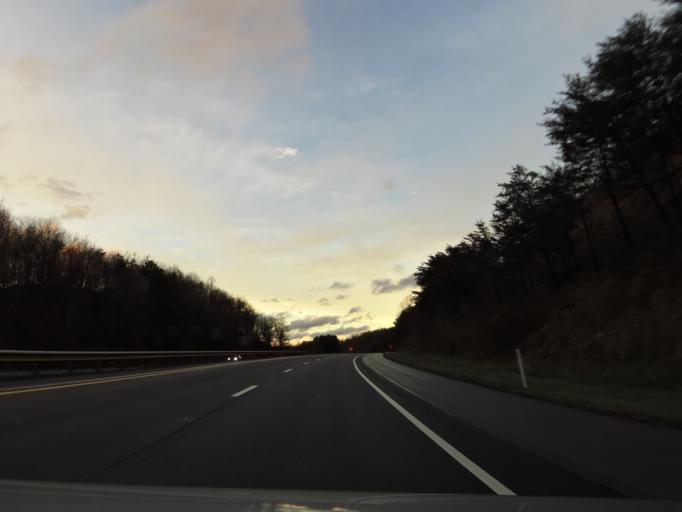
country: US
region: Tennessee
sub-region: Campbell County
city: Jacksboro
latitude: 36.3971
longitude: -84.2617
